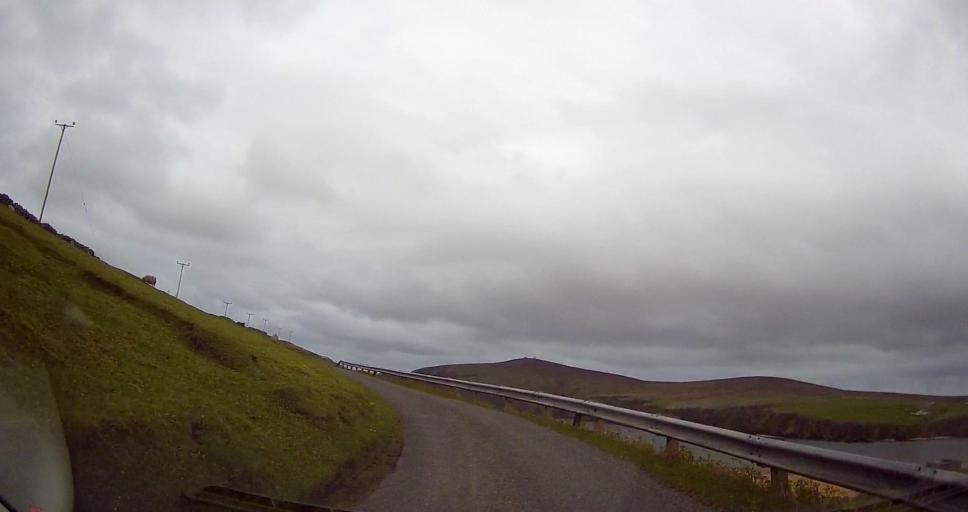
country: GB
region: Scotland
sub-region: Shetland Islands
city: Shetland
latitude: 60.8056
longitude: -0.8818
